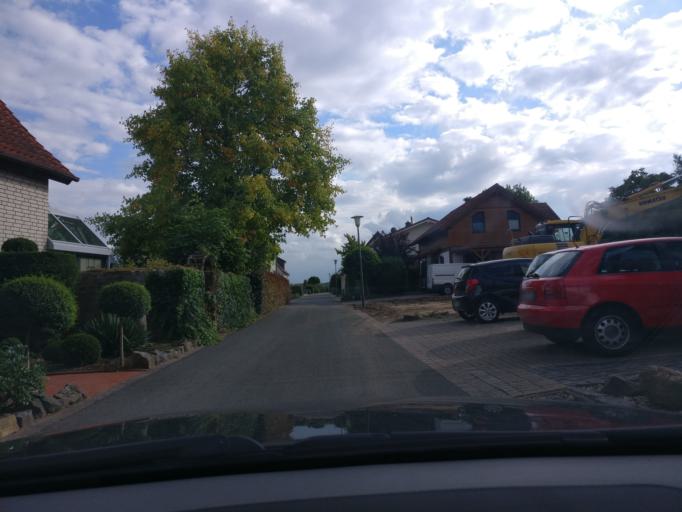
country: DE
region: Lower Saxony
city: Melle
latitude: 52.1878
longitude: 8.3451
